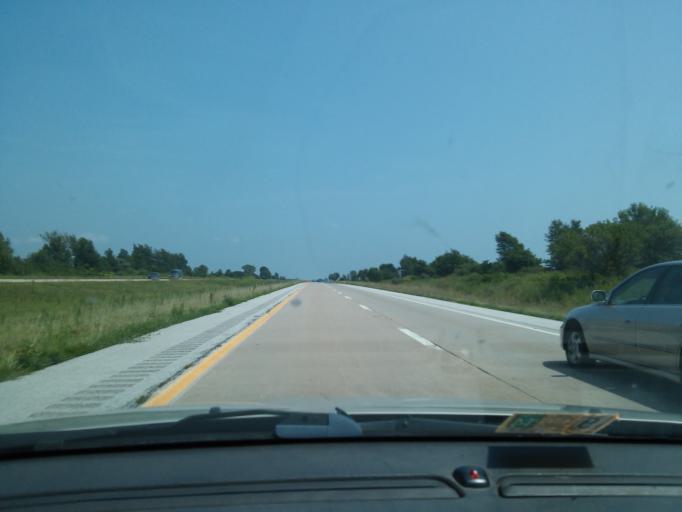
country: US
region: Illinois
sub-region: Scott County
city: Winchester
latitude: 39.6810
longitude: -90.4913
